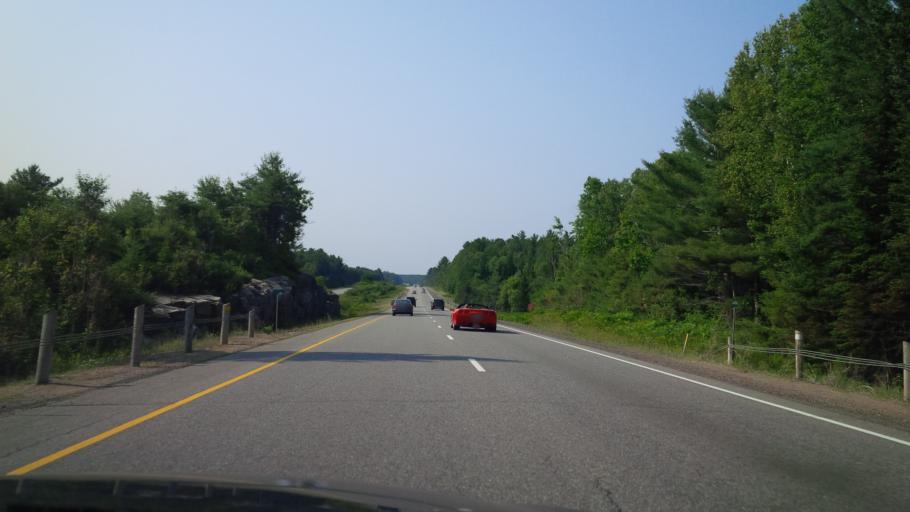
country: CA
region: Ontario
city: Bracebridge
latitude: 45.1331
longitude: -79.3113
